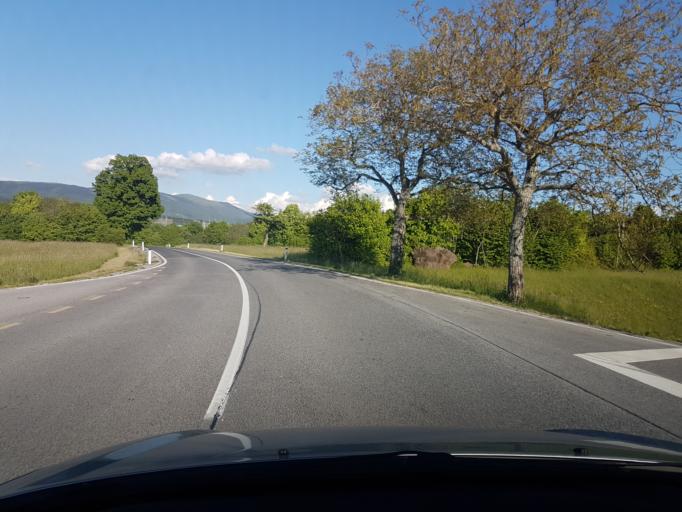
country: SI
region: Divaca
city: Divaca
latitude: 45.6940
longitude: 13.9524
